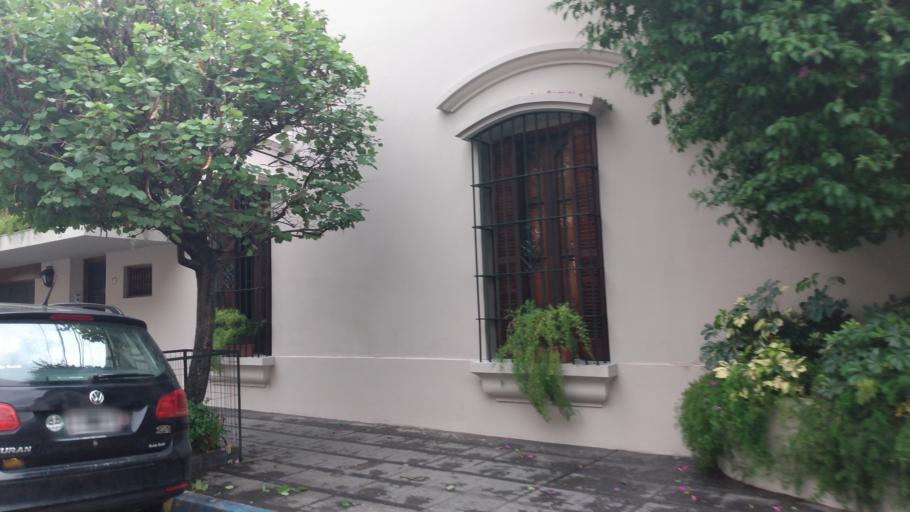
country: AR
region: Corrientes
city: Corrientes
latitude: -27.4662
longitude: -58.8399
